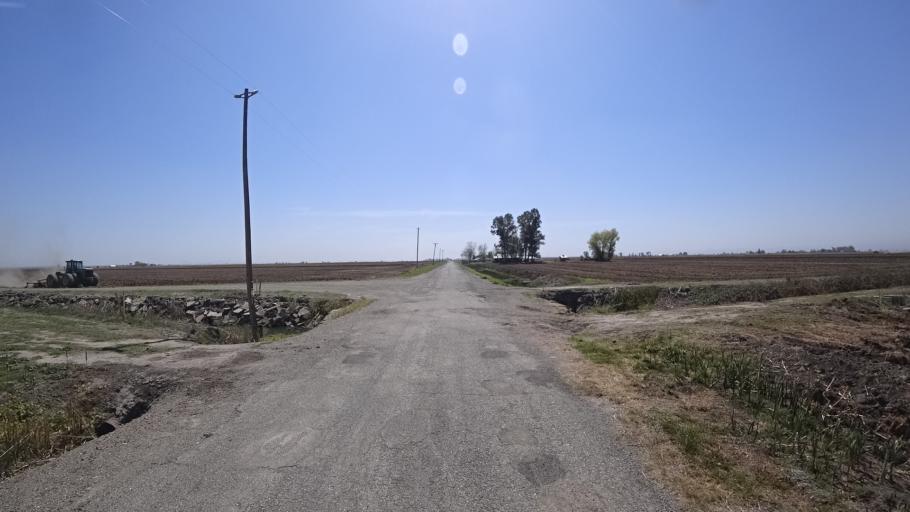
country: US
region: California
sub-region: Glenn County
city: Willows
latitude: 39.5347
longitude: -122.0980
